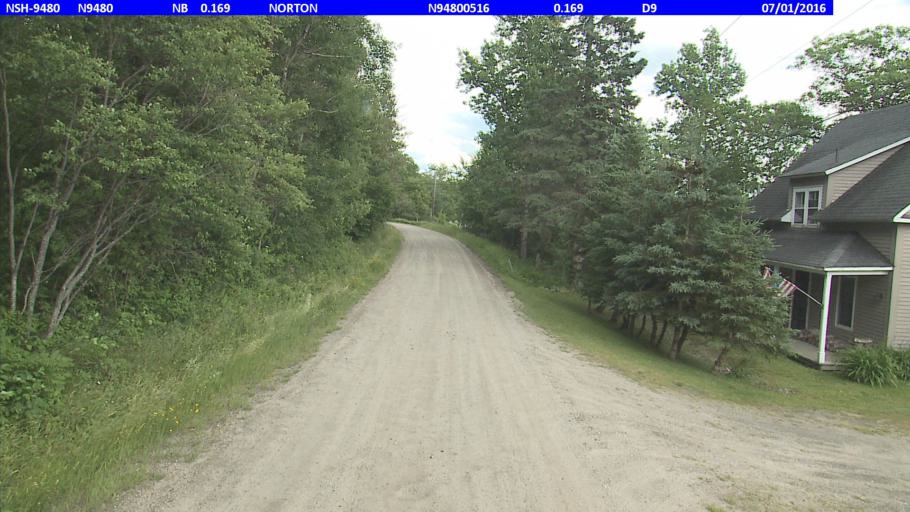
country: CA
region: Quebec
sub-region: Estrie
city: Coaticook
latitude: 44.9946
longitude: -71.7145
